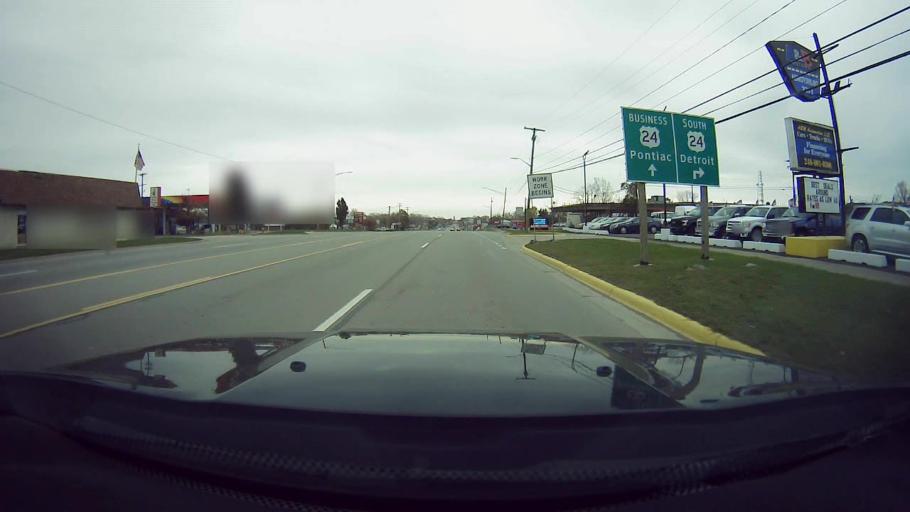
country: US
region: Michigan
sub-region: Oakland County
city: Pontiac
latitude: 42.6687
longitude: -83.3335
